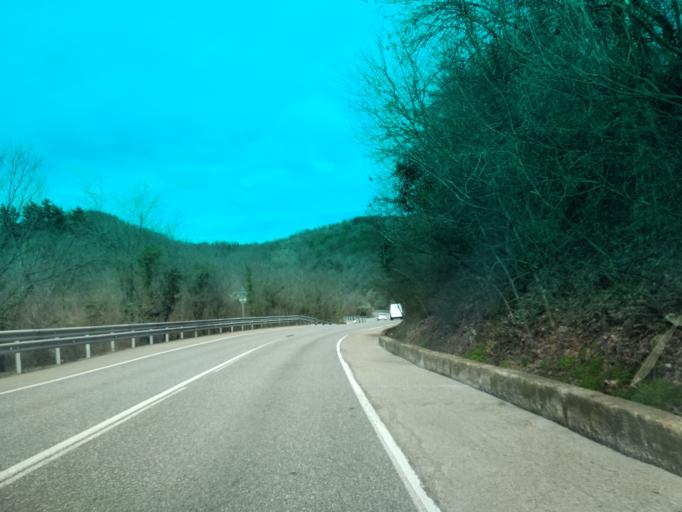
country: RU
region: Krasnodarskiy
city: Shepsi
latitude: 44.0456
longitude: 39.1332
